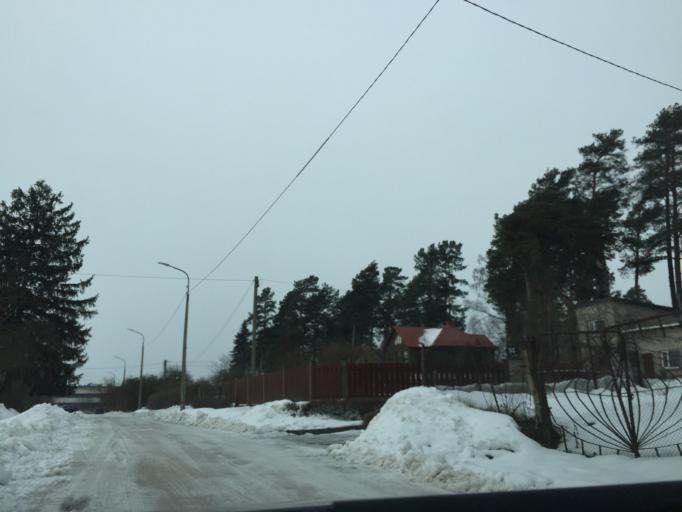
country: LV
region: Ogre
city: Ogre
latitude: 56.8216
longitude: 24.5741
